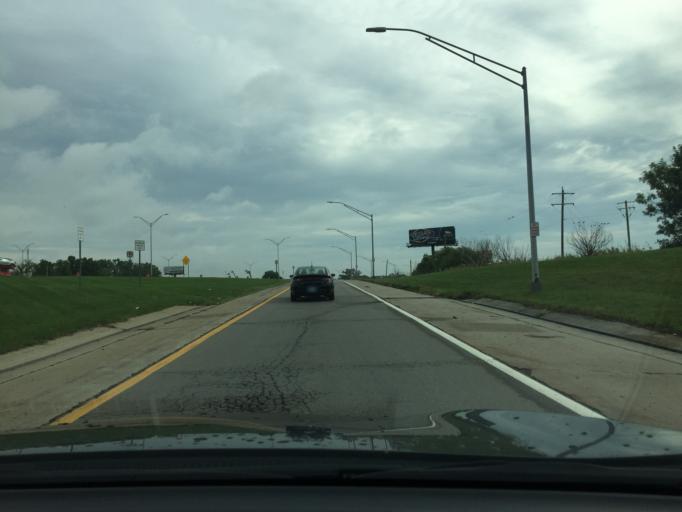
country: US
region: Michigan
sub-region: Wayne County
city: Inkster
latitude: 42.2416
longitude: -83.3270
